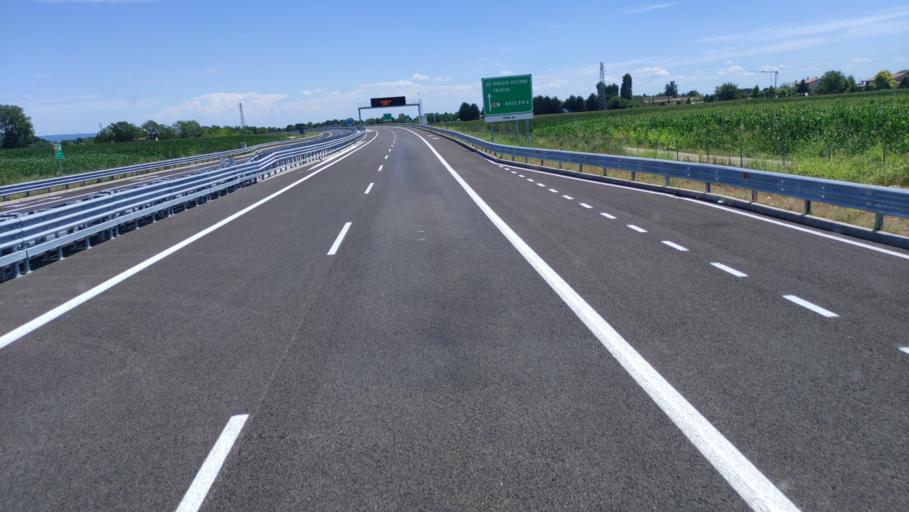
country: IT
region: Veneto
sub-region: Provincia di Treviso
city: Ca' Rainati
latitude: 45.7464
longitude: 11.8436
